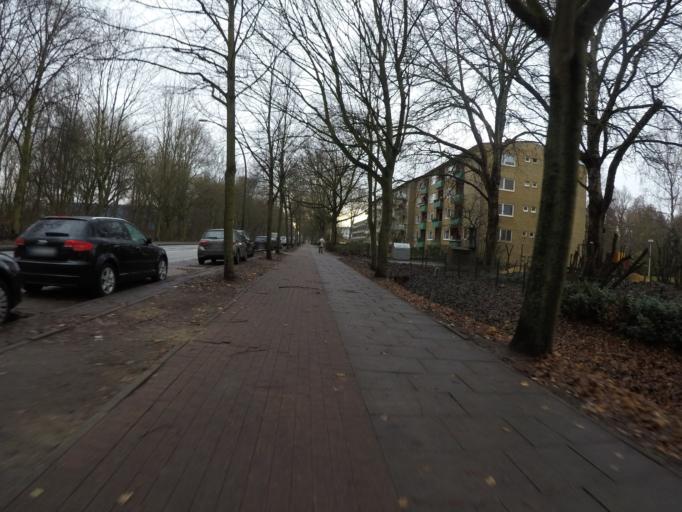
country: DE
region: Hamburg
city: Harburg
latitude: 53.4896
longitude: 9.9903
